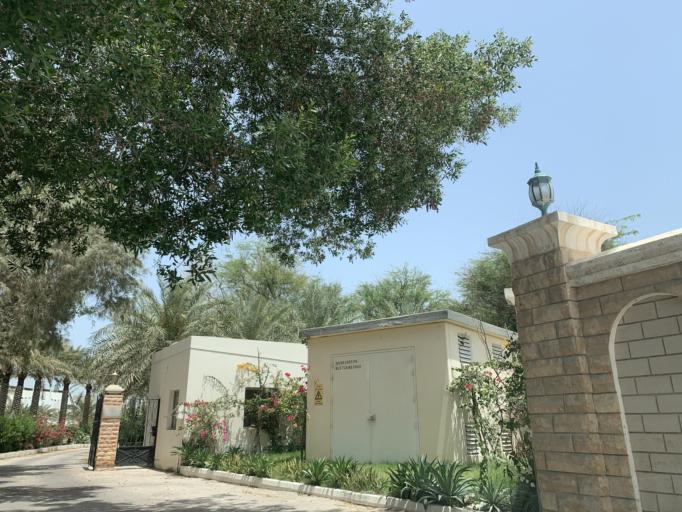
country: BH
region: Northern
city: Madinat `Isa
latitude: 26.1723
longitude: 50.5719
